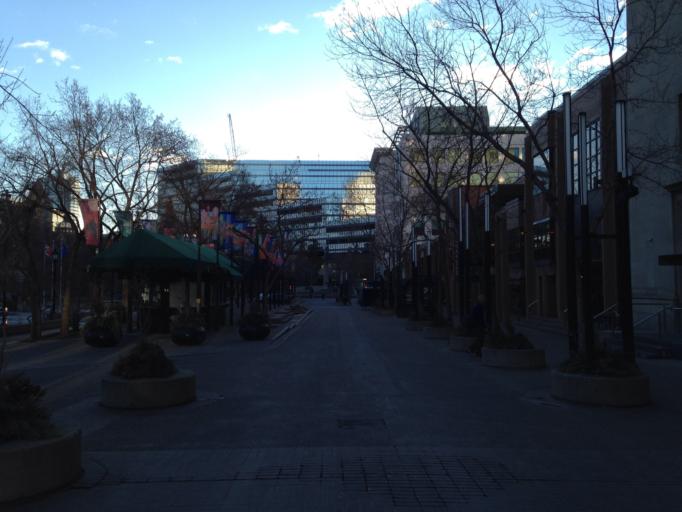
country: CA
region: Alberta
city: Calgary
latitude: 51.0454
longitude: -114.0602
